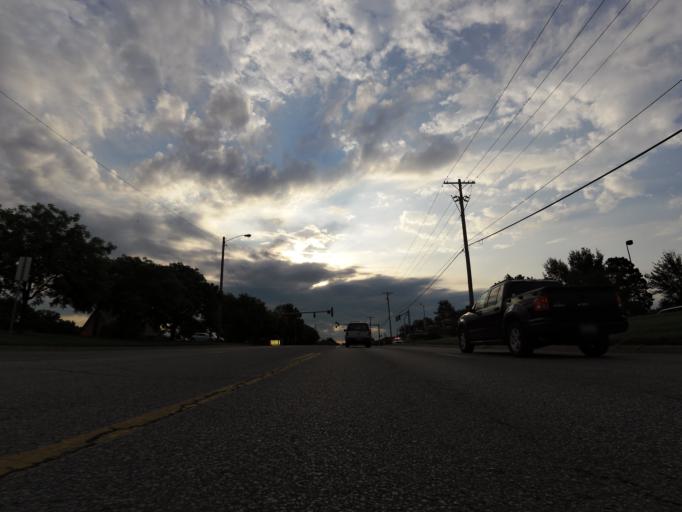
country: US
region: Kansas
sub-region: Sedgwick County
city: Bellaire
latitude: 37.7228
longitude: -97.2947
